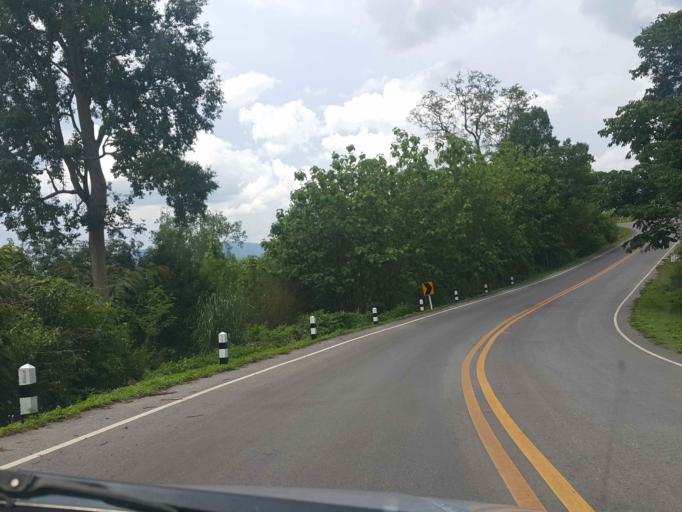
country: TH
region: Nan
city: Ban Luang
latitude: 18.8599
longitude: 100.4556
